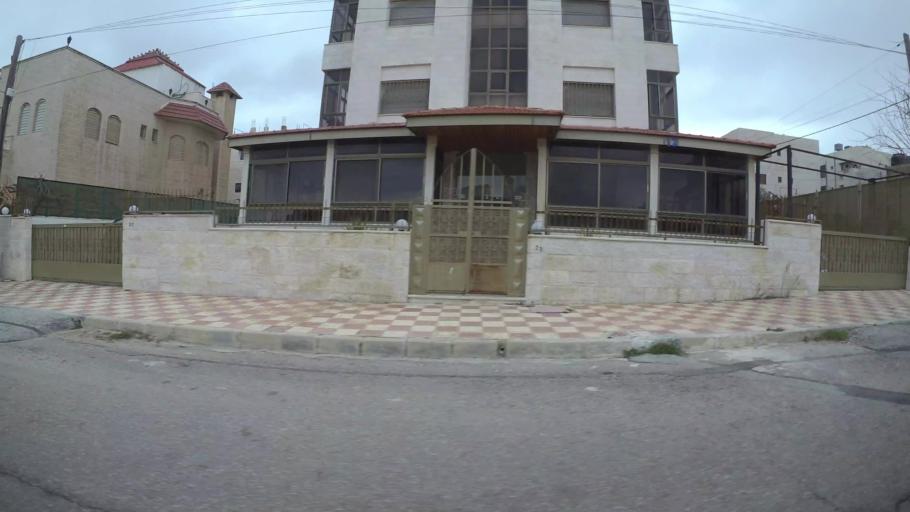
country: JO
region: Amman
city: Al Jubayhah
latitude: 31.9936
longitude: 35.8433
